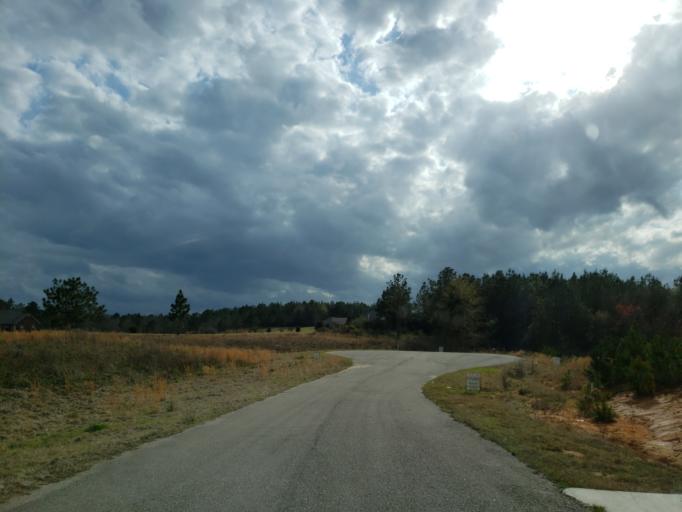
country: US
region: Mississippi
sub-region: Jones County
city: Ellisville
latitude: 31.5530
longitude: -89.2592
